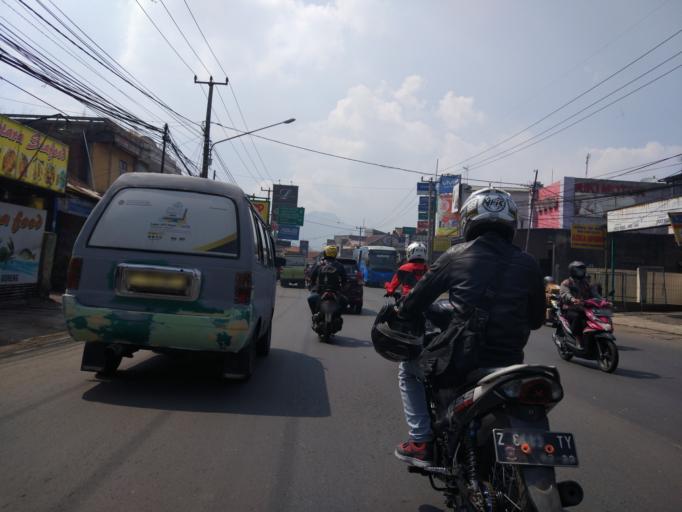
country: ID
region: West Java
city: Cileunyi
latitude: -6.9400
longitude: 107.7509
